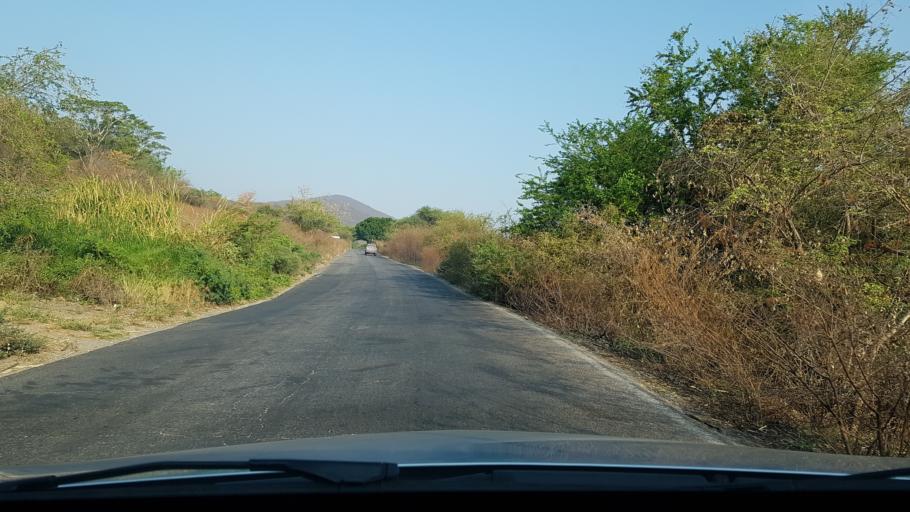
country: MX
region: Morelos
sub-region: Tepalcingo
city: Zacapalco
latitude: 18.6517
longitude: -99.0306
